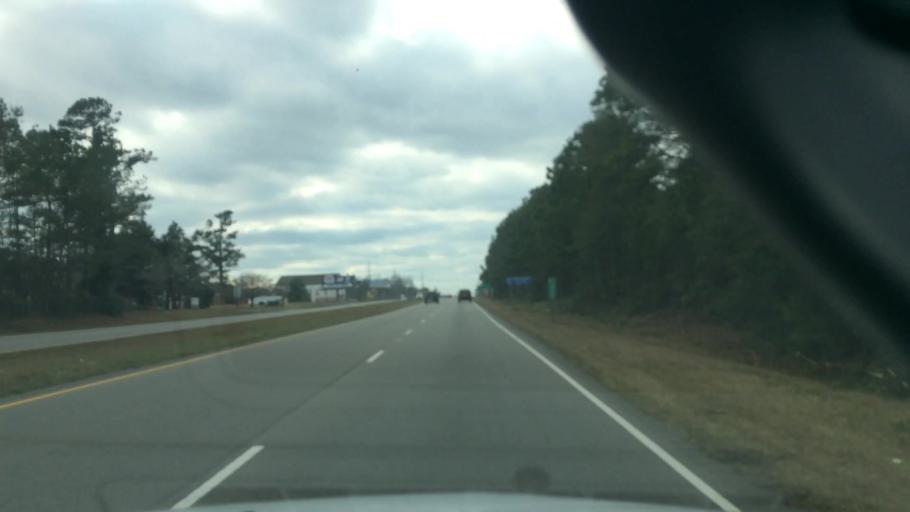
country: US
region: North Carolina
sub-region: Brunswick County
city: Shallotte
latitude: 34.0191
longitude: -78.2687
